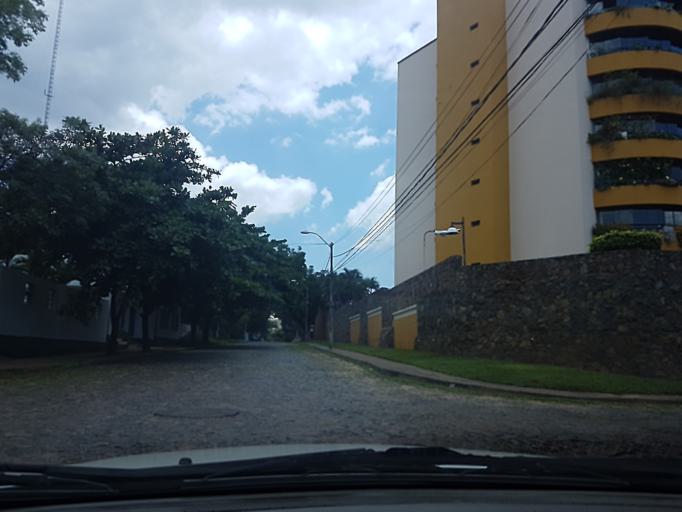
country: PY
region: Central
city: Fernando de la Mora
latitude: -25.2787
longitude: -57.5638
